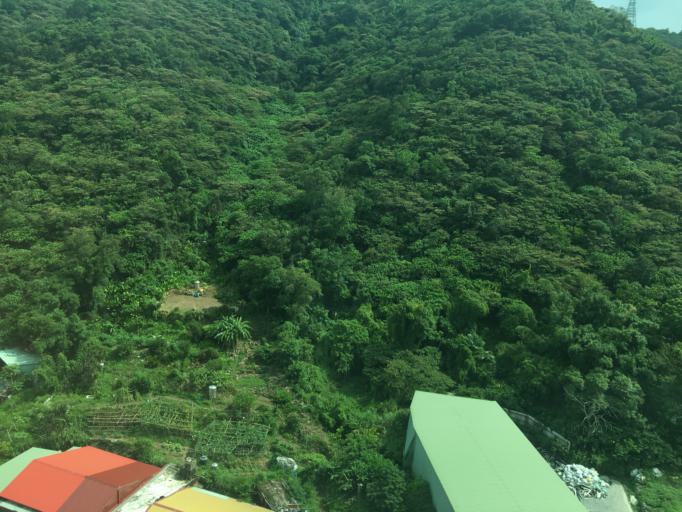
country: TW
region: Taipei
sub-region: Taipei
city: Banqiao
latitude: 25.0289
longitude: 121.4054
